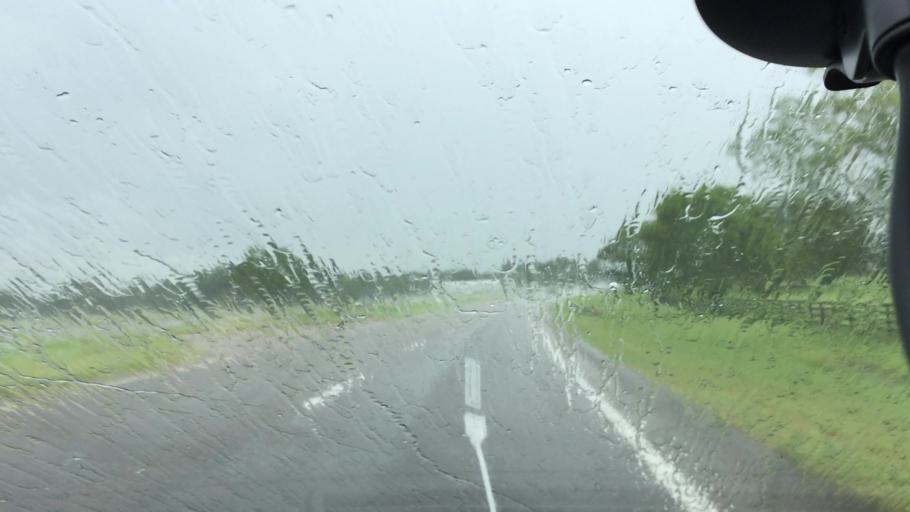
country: US
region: Alabama
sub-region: Montgomery County
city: Pike Road
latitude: 32.2264
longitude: -86.1186
